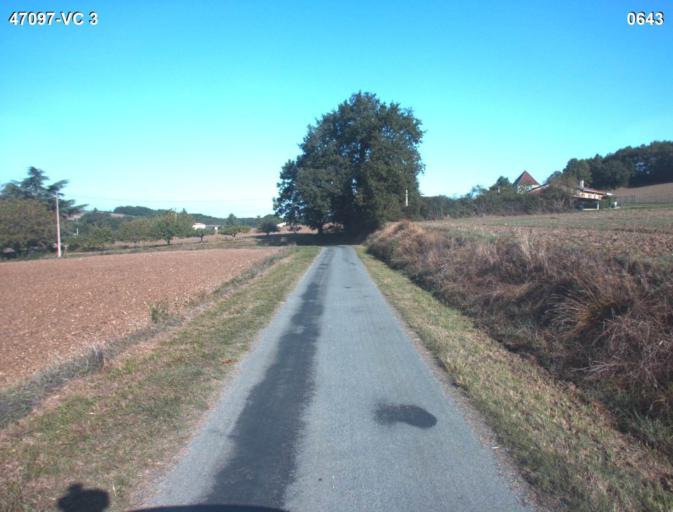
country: FR
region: Aquitaine
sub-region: Departement du Lot-et-Garonne
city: Vianne
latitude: 44.1949
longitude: 0.3594
